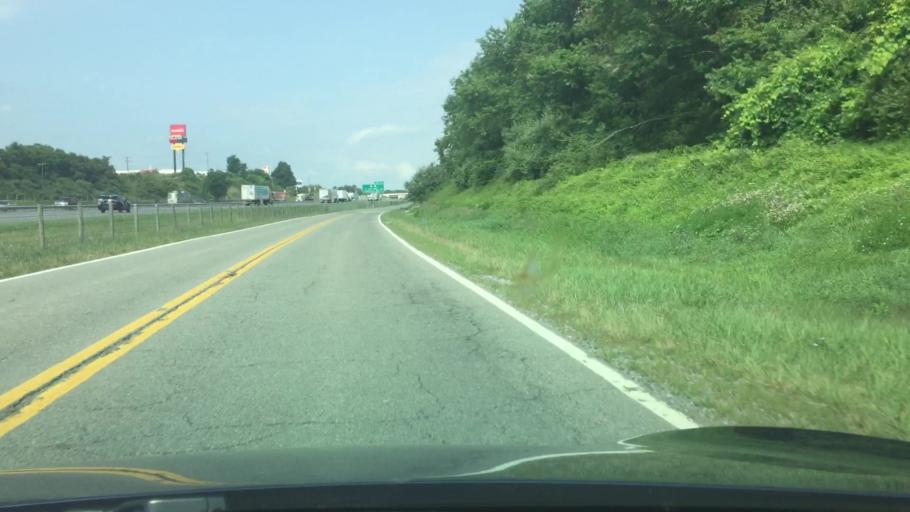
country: US
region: Virginia
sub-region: Wythe County
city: Wytheville
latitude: 36.9334
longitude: -80.9884
